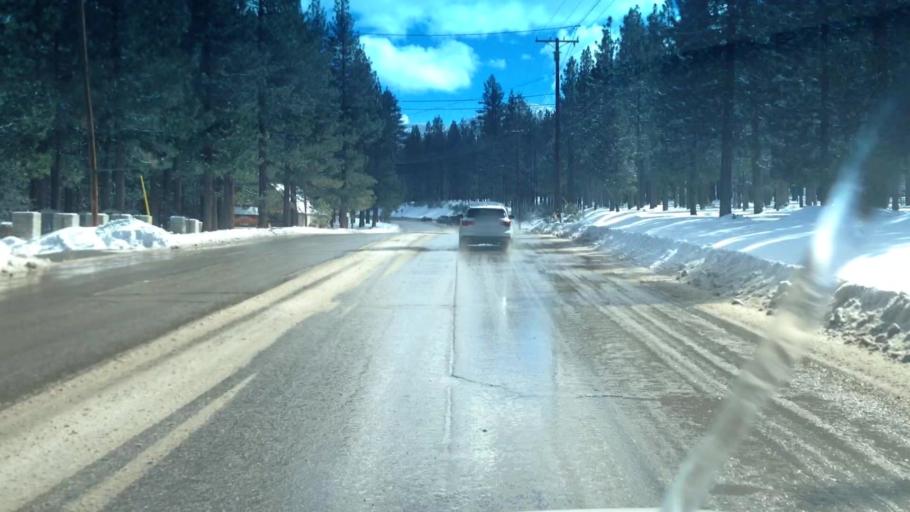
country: US
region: California
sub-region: San Bernardino County
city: Big Bear Lake
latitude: 34.2428
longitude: -116.8811
